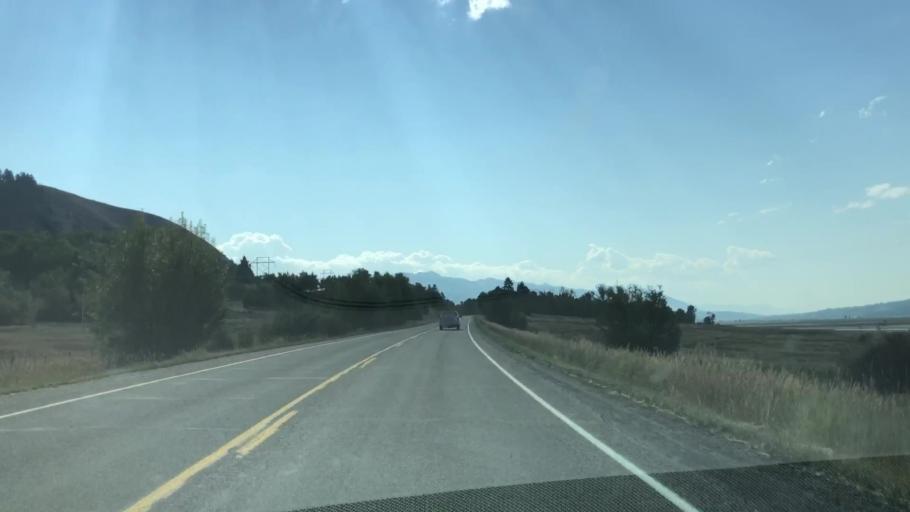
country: US
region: Wyoming
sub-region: Teton County
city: Hoback
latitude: 43.2146
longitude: -111.0624
